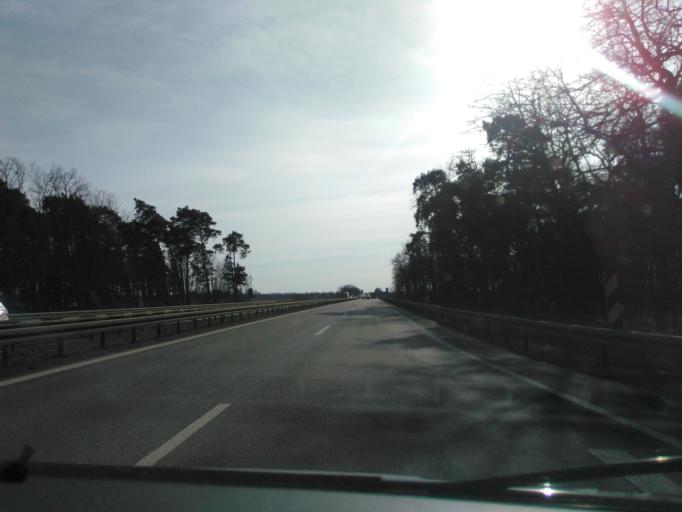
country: DE
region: Brandenburg
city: Calau
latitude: 51.7842
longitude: 13.8759
